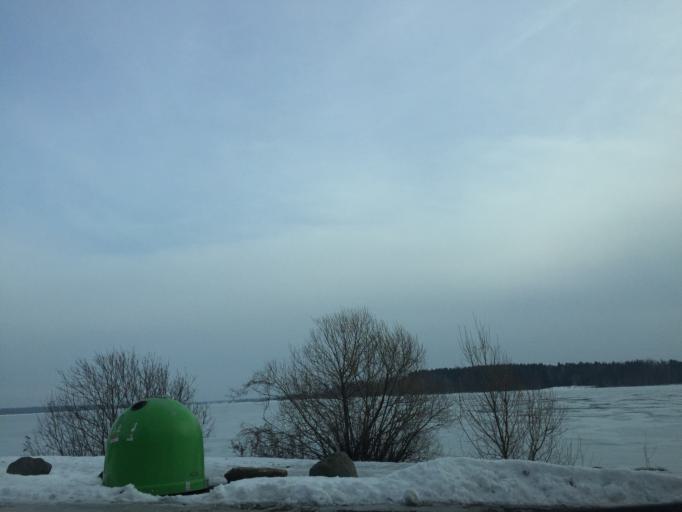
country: LV
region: Ikskile
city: Ikskile
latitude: 56.8421
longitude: 24.4325
